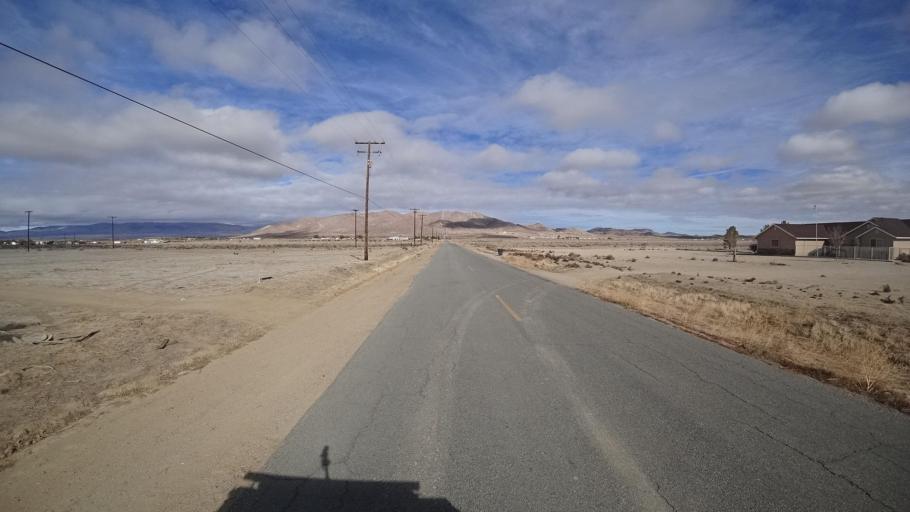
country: US
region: California
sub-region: Kern County
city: Rosamond
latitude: 34.8555
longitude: -118.2733
